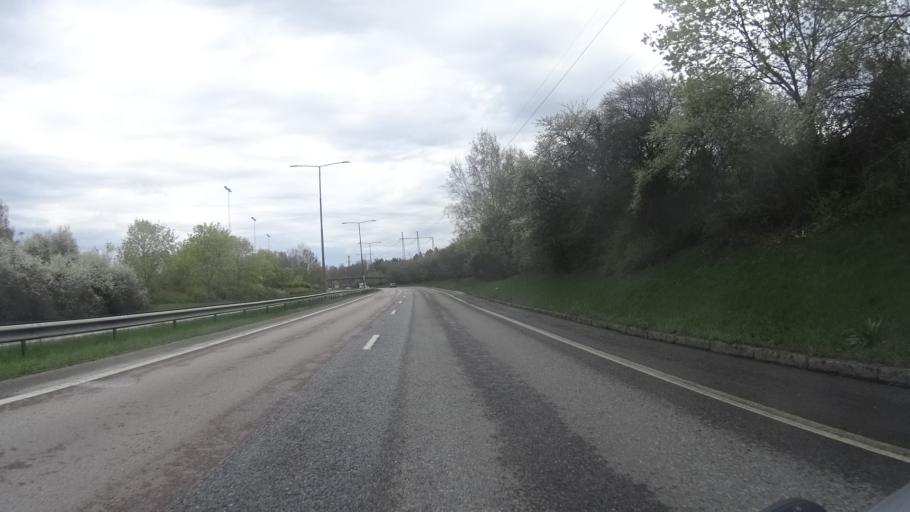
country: SE
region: Stockholm
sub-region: Stockholms Kommun
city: Arsta
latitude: 59.2775
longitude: 18.0394
